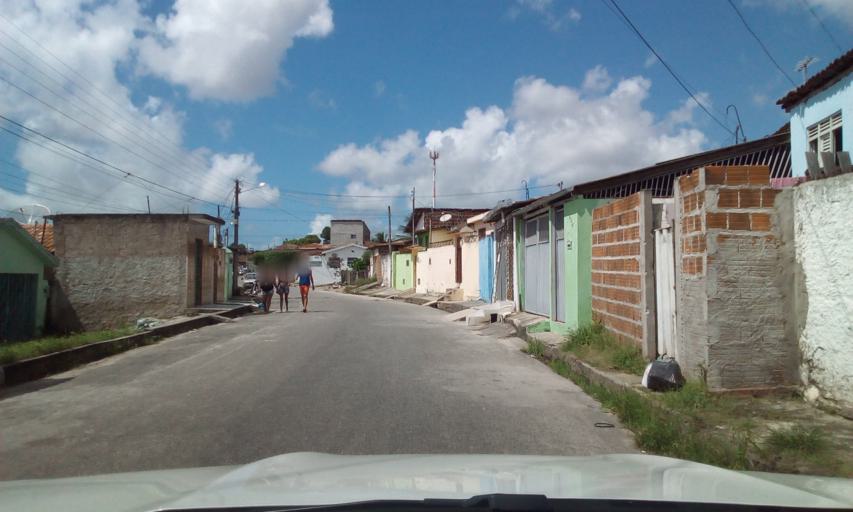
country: BR
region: Paraiba
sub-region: Bayeux
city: Bayeux
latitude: -7.1327
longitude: -34.9237
